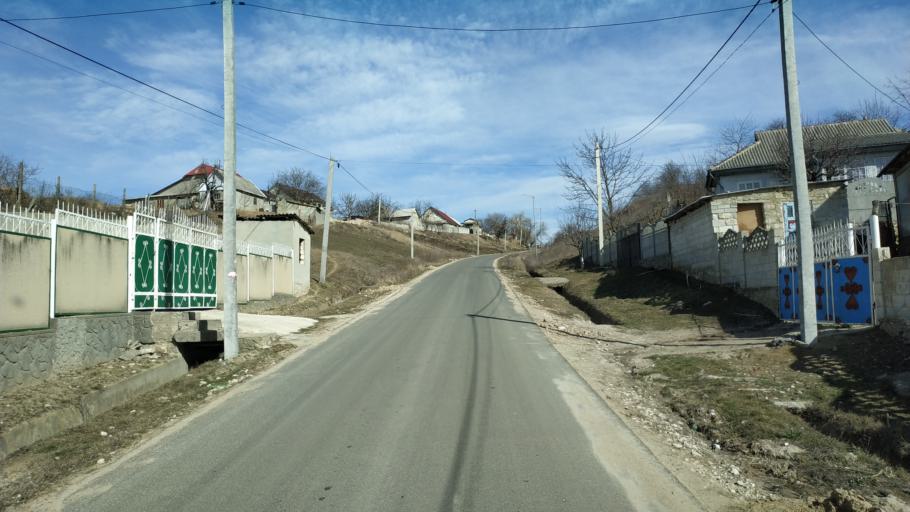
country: MD
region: Nisporeni
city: Nisporeni
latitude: 47.0995
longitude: 28.2938
